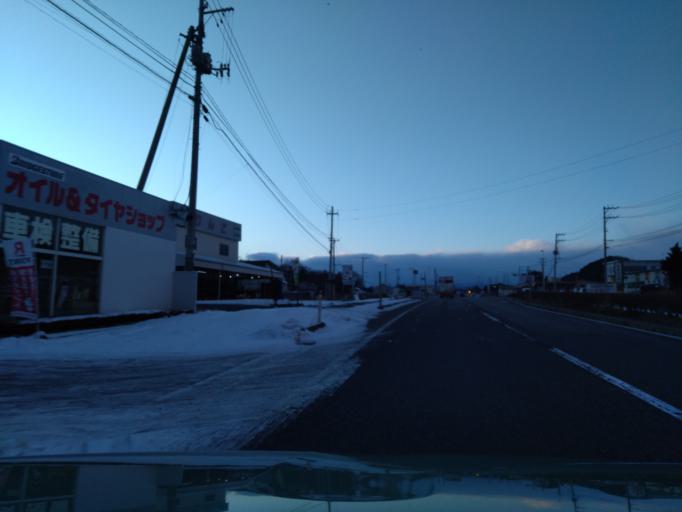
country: JP
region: Iwate
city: Shizukuishi
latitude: 39.6996
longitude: 141.0550
